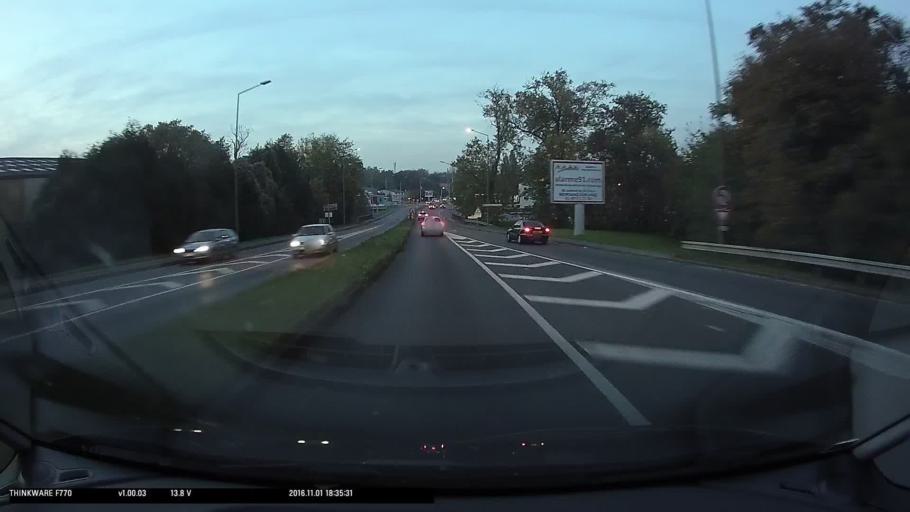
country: FR
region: Ile-de-France
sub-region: Departement de l'Essonne
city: Villemoisson-sur-Orge
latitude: 48.6667
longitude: 2.3394
